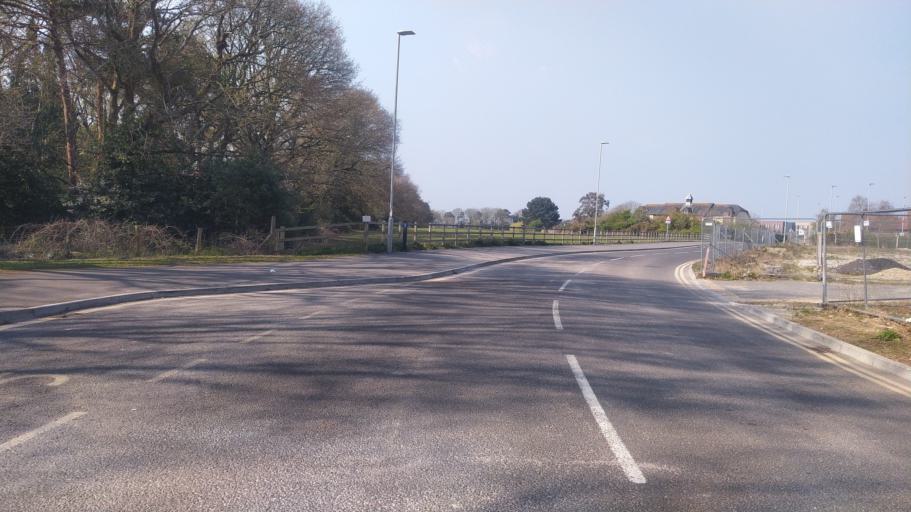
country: GB
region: England
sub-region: Bournemouth
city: Bournemouth
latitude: 50.7414
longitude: -1.8929
